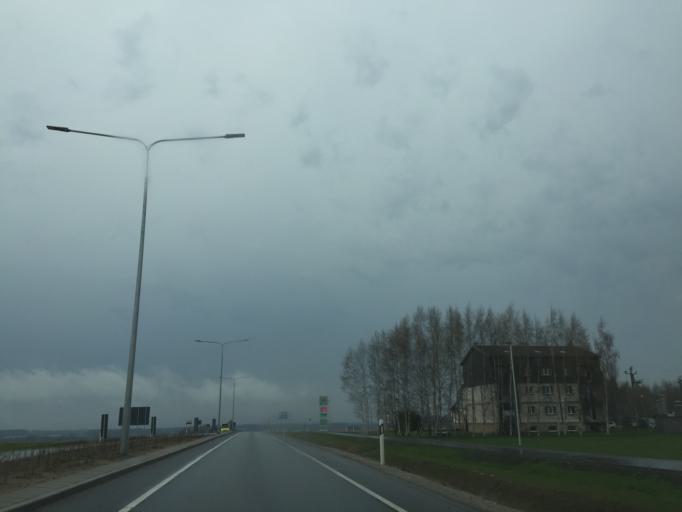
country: EE
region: Tartu
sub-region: UElenurme vald
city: Ulenurme
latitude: 58.2382
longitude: 26.6901
